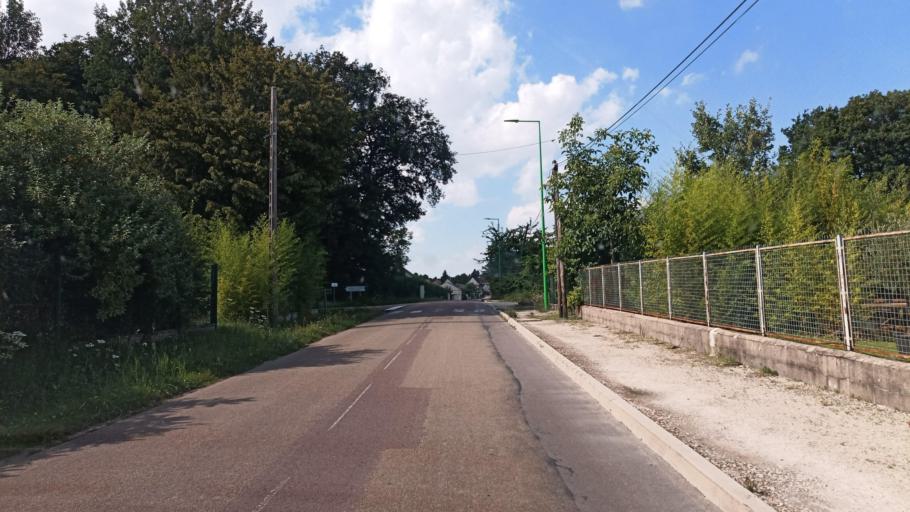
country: FR
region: Bourgogne
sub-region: Departement de l'Yonne
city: Saint-Valerien
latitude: 48.1739
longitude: 3.0984
